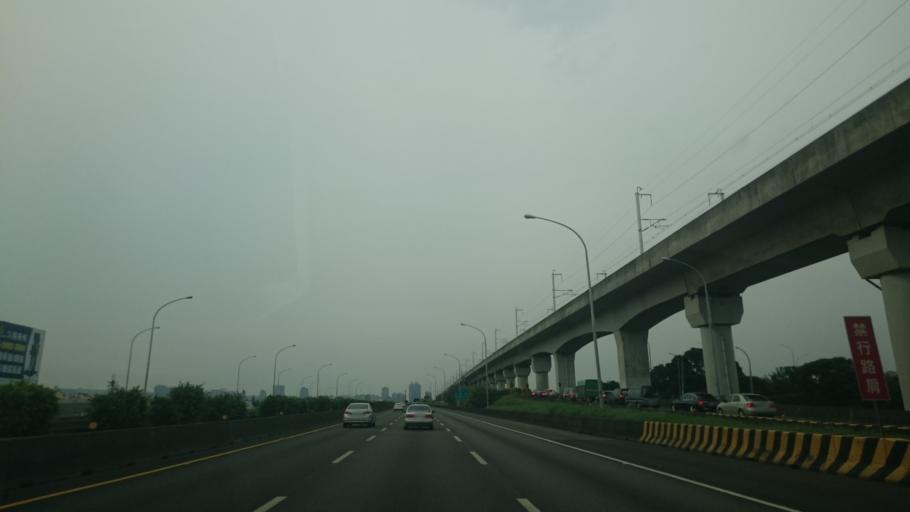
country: TW
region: Taiwan
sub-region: Taichung City
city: Taichung
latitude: 24.1482
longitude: 120.6195
